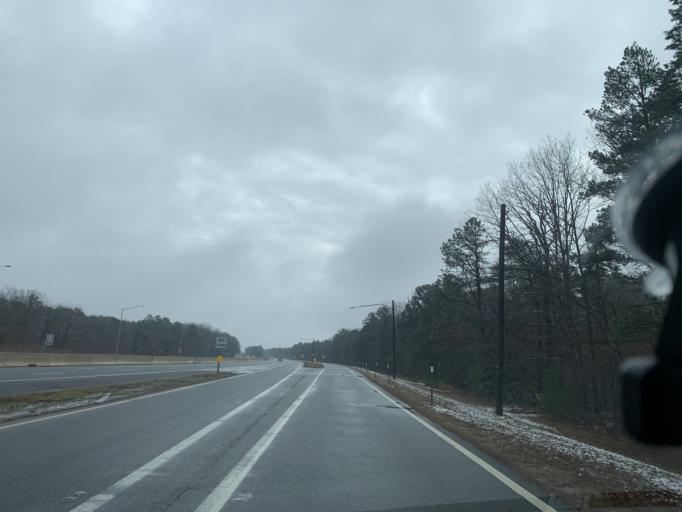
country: US
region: New Jersey
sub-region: Atlantic County
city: Pomona
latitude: 39.4468
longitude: -74.6208
